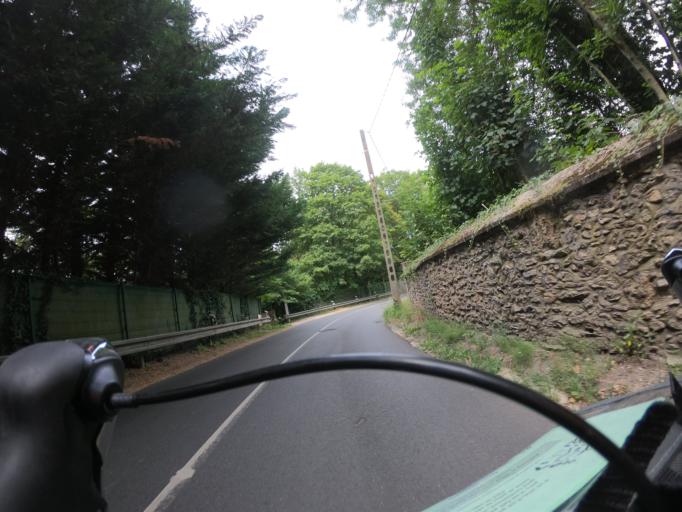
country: FR
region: Ile-de-France
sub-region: Departement de l'Essonne
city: Igny
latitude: 48.7499
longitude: 2.2272
